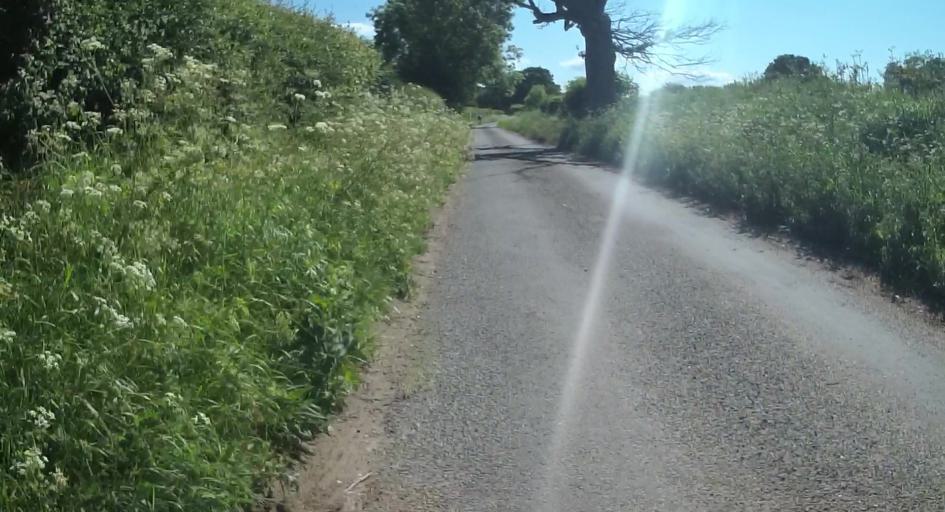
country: GB
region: England
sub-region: Hampshire
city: Old Basing
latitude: 51.2487
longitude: -1.0276
